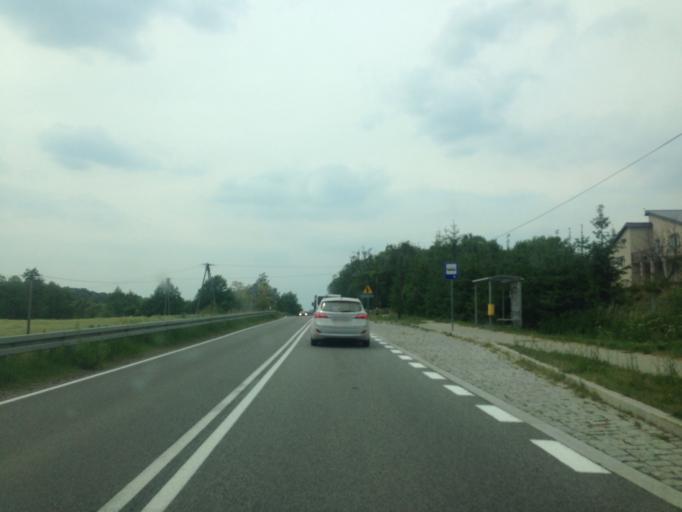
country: PL
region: Kujawsko-Pomorskie
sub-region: Powiat grudziadzki
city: Rogozno
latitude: 53.5007
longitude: 18.8785
